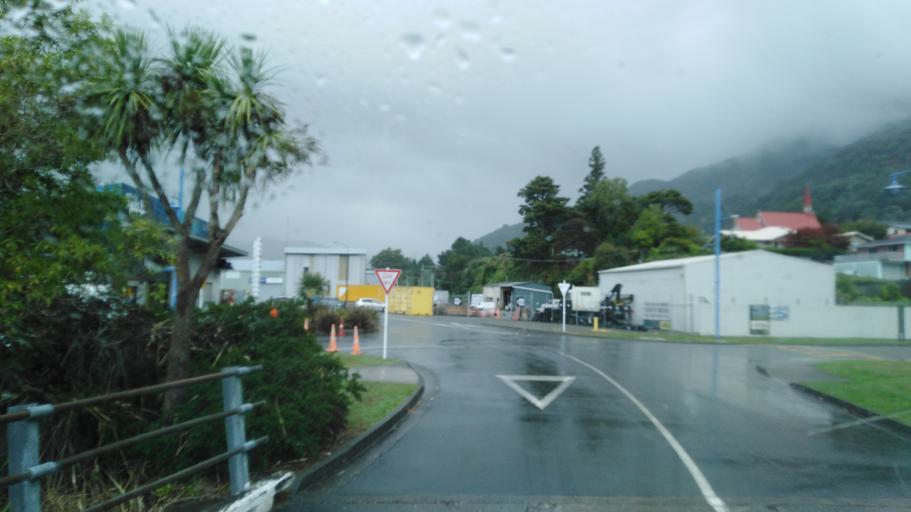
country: NZ
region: Marlborough
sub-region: Marlborough District
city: Picton
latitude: -41.2788
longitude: 173.7691
